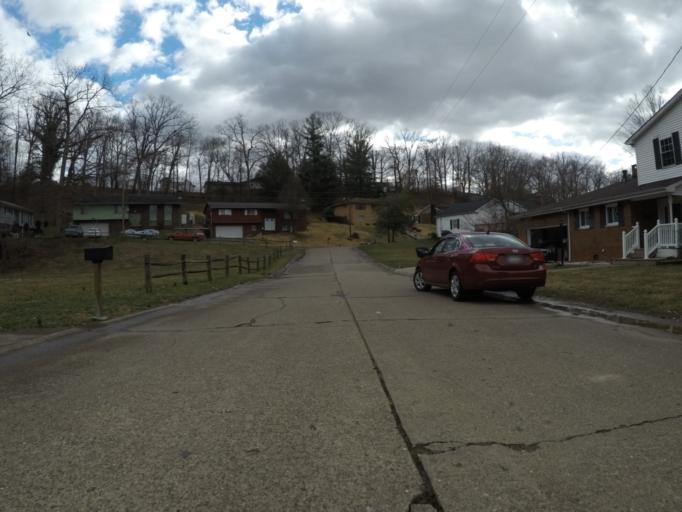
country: US
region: West Virginia
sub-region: Cabell County
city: Pea Ridge
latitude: 38.4075
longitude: -82.3823
